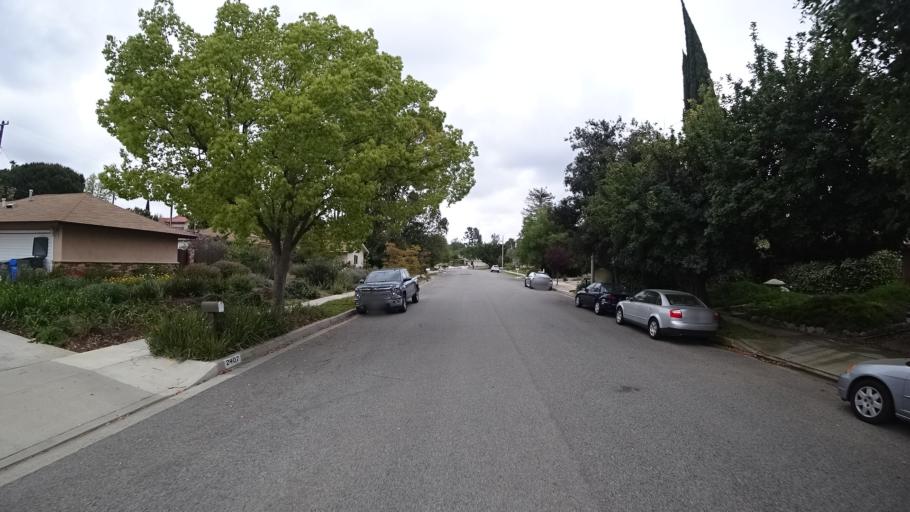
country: US
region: California
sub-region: Ventura County
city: Thousand Oaks
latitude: 34.2155
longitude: -118.8805
